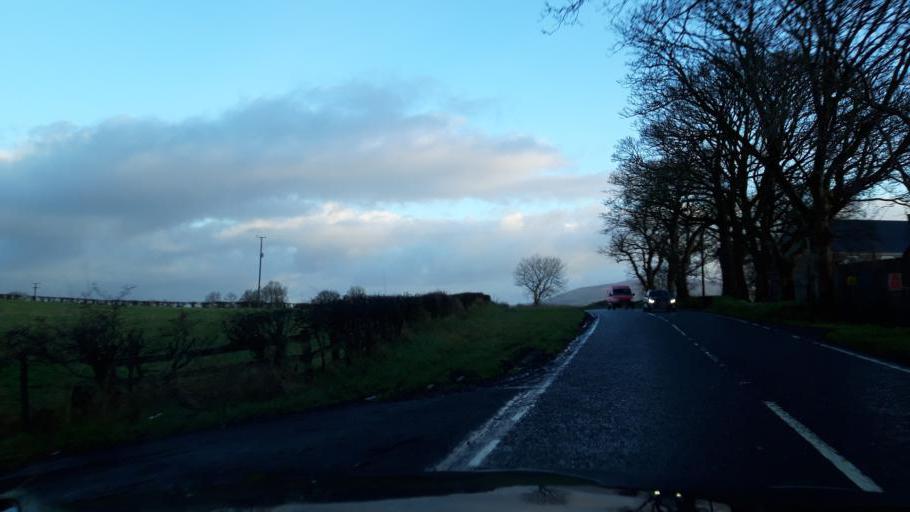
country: GB
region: Northern Ireland
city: Dunloy
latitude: 55.1064
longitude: -6.3435
